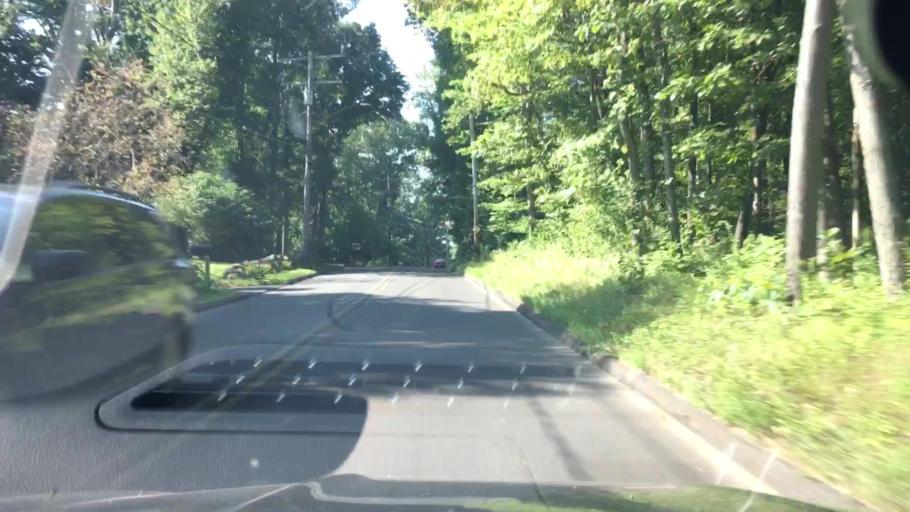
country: US
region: Connecticut
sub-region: New Haven County
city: Cheshire Village
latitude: 41.5260
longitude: -72.9122
